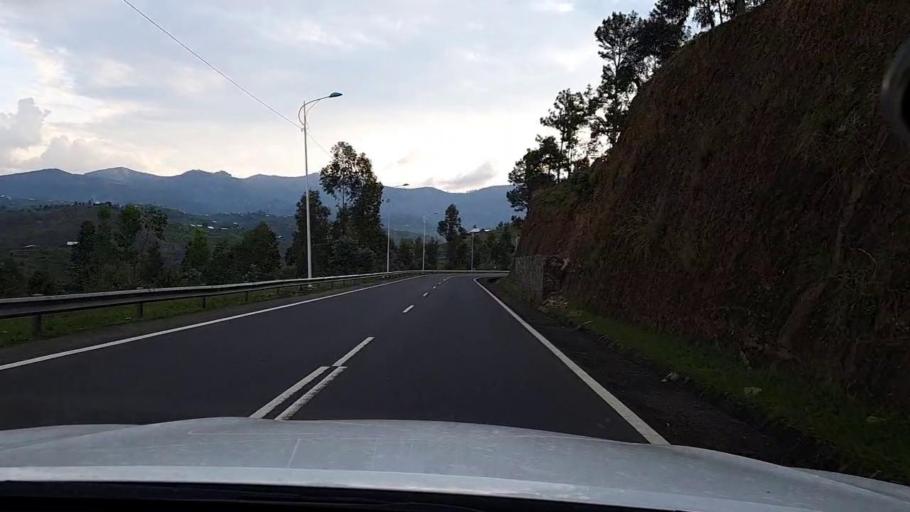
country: RW
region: Western Province
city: Kibuye
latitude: -2.0871
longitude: 29.4056
